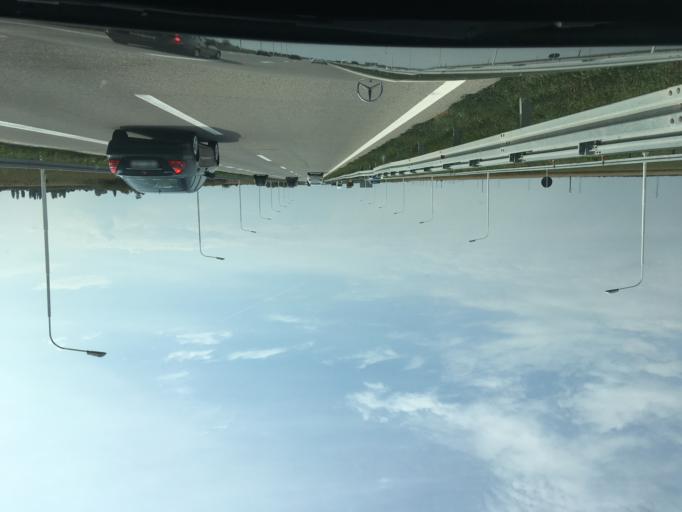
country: RS
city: Ravnje
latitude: 45.0356
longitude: 19.4505
